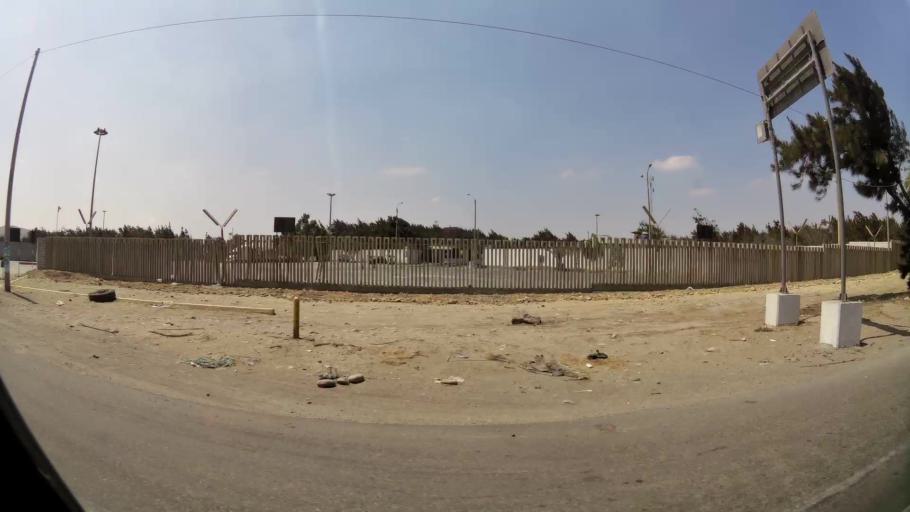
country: PE
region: La Libertad
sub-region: Provincia de Pacasmayo
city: Pacasmayo
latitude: -7.4030
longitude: -79.5584
